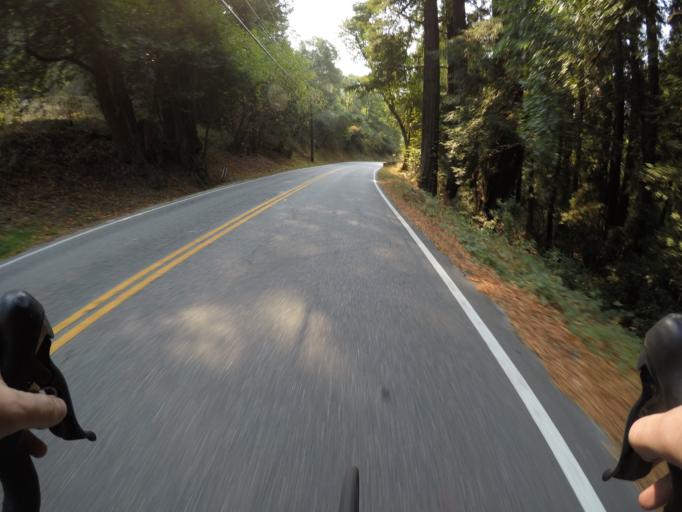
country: US
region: California
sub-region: Santa Cruz County
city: Pasatiempo
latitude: 37.0056
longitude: -122.0099
